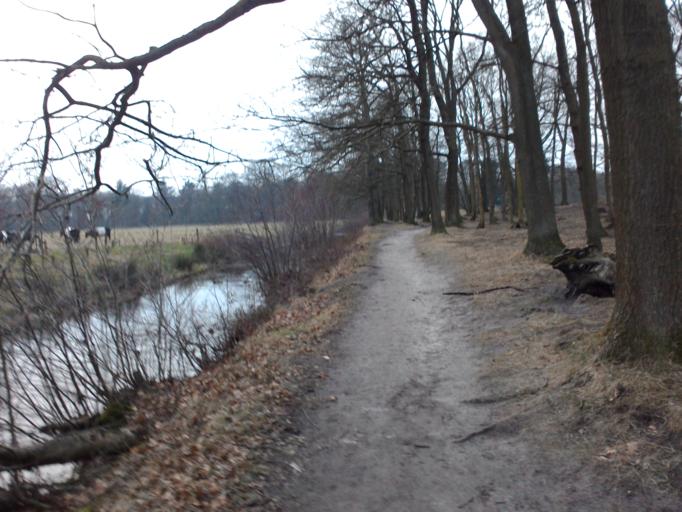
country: NL
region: Utrecht
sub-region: Gemeente De Bilt
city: De Bilt
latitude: 52.1109
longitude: 5.1973
